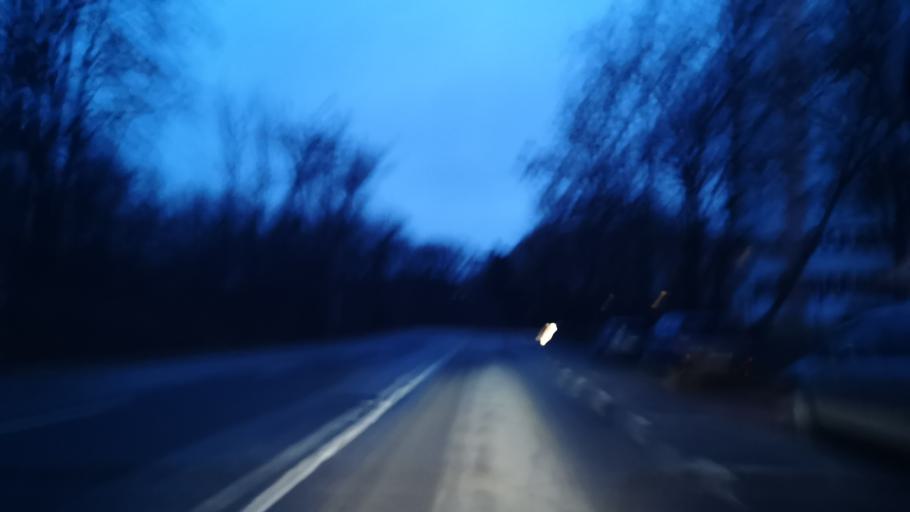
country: MD
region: Chisinau
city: Chisinau
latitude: 47.0385
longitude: 28.8793
